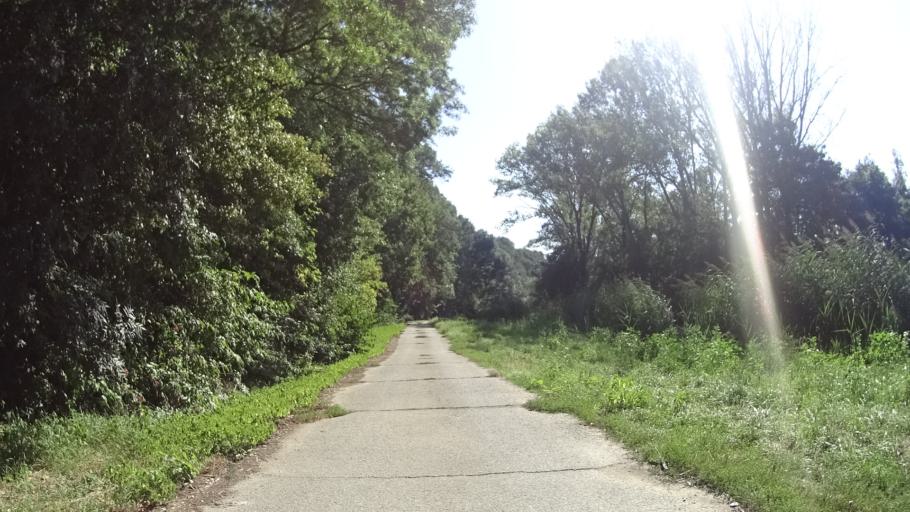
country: CZ
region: South Moravian
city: Hodonin
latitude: 48.8167
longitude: 17.1204
